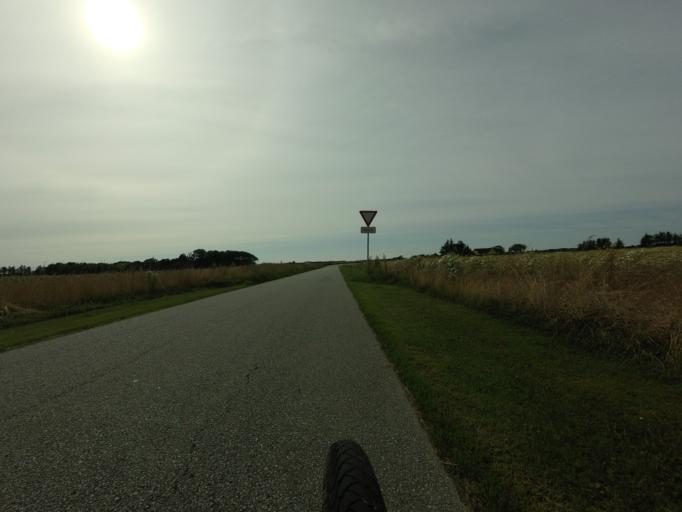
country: DK
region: North Denmark
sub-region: Hjorring Kommune
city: Hjorring
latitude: 57.4351
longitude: 9.8737
